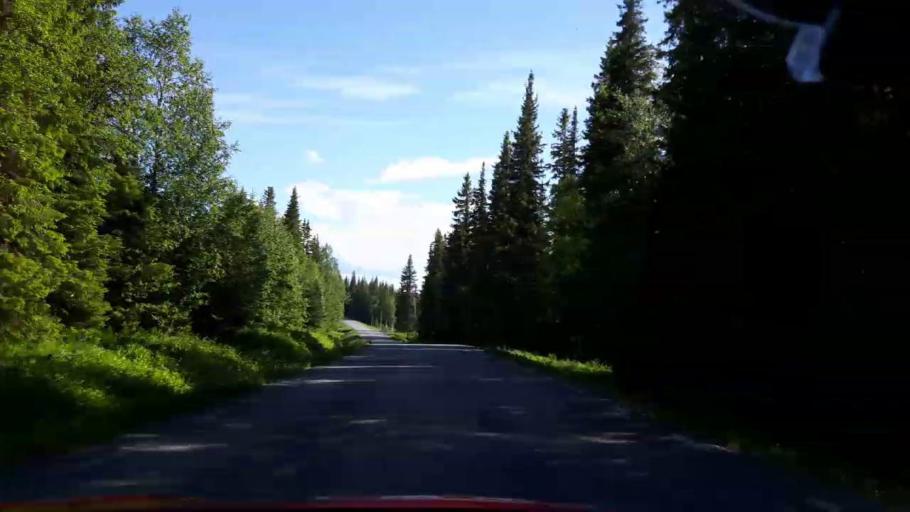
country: SE
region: Jaemtland
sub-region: Krokoms Kommun
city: Valla
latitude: 63.7258
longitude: 14.1221
